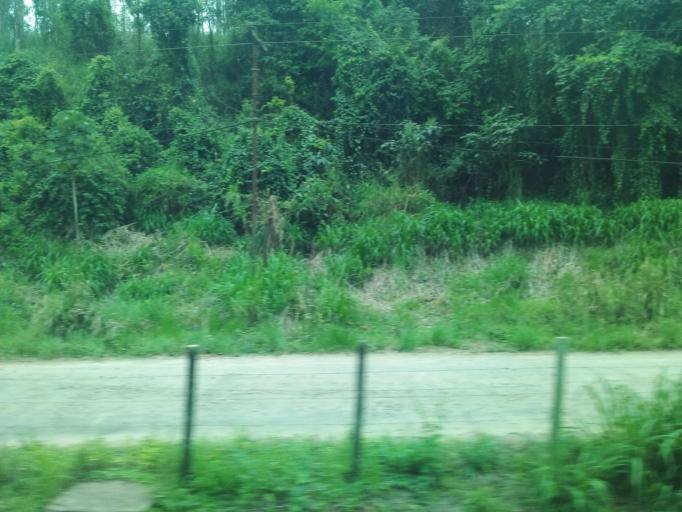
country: BR
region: Minas Gerais
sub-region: Nova Era
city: Nova Era
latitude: -19.7249
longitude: -42.9897
